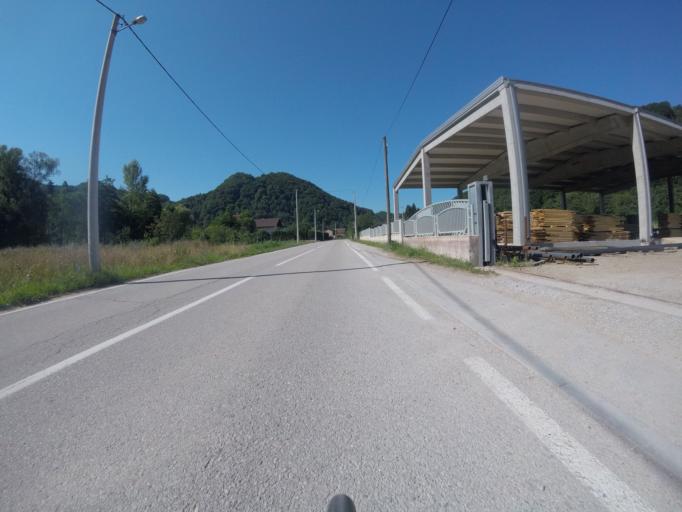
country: HR
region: Zagrebacka
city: Bregana
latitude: 45.8269
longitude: 15.6496
